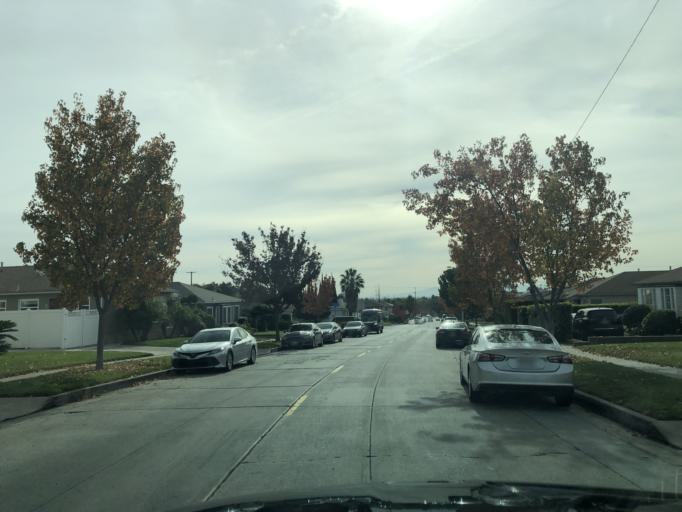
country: US
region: California
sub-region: Los Angeles County
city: Ladera Heights
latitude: 33.9850
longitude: -118.3615
